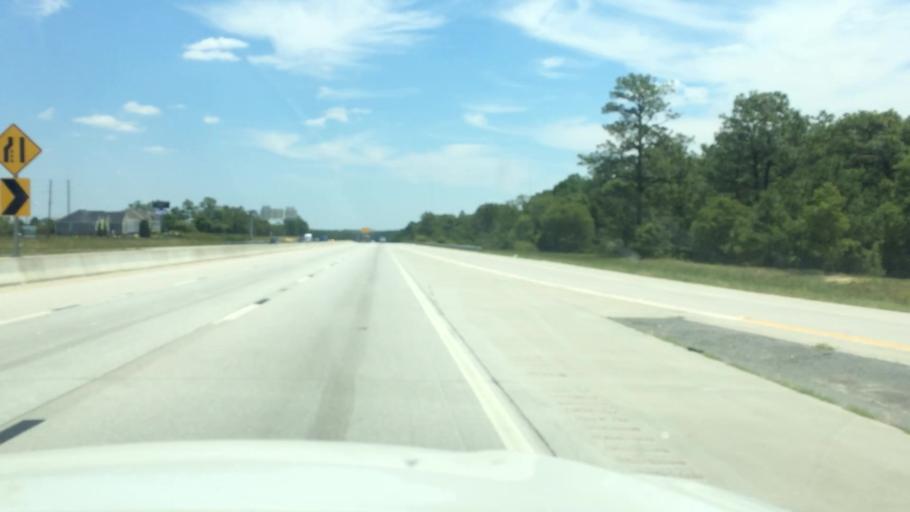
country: US
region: South Carolina
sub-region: Kershaw County
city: Elgin
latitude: 34.1053
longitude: -80.8272
